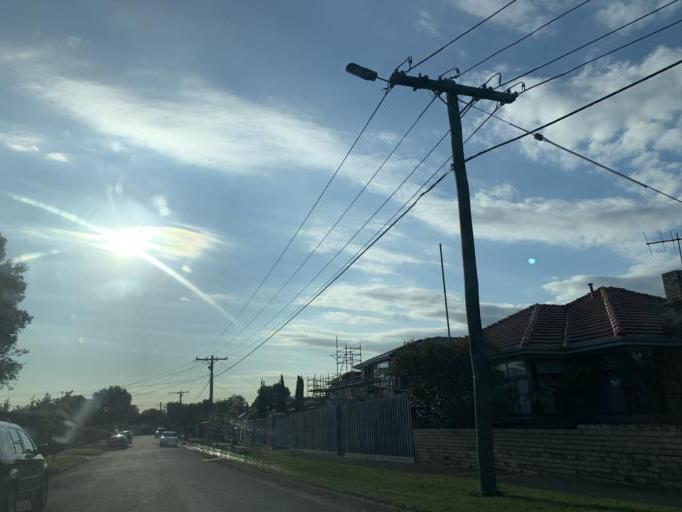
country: AU
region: Victoria
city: Heatherton
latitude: -37.9814
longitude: 145.0932
